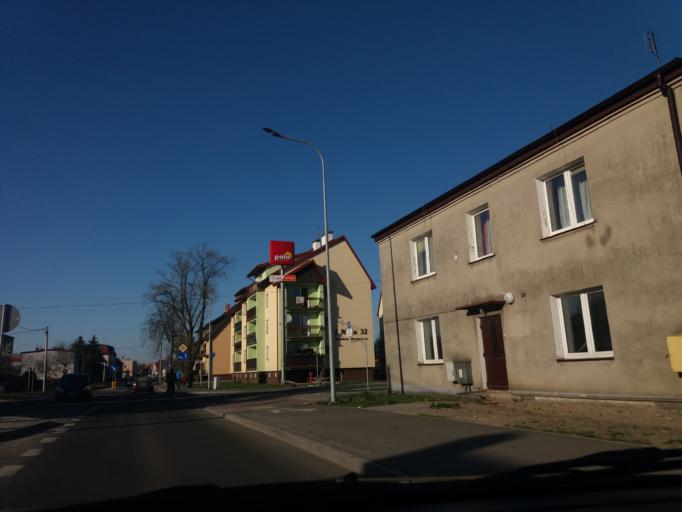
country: PL
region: Warmian-Masurian Voivodeship
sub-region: Powiat nidzicki
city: Nidzica
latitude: 53.3646
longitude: 20.4276
